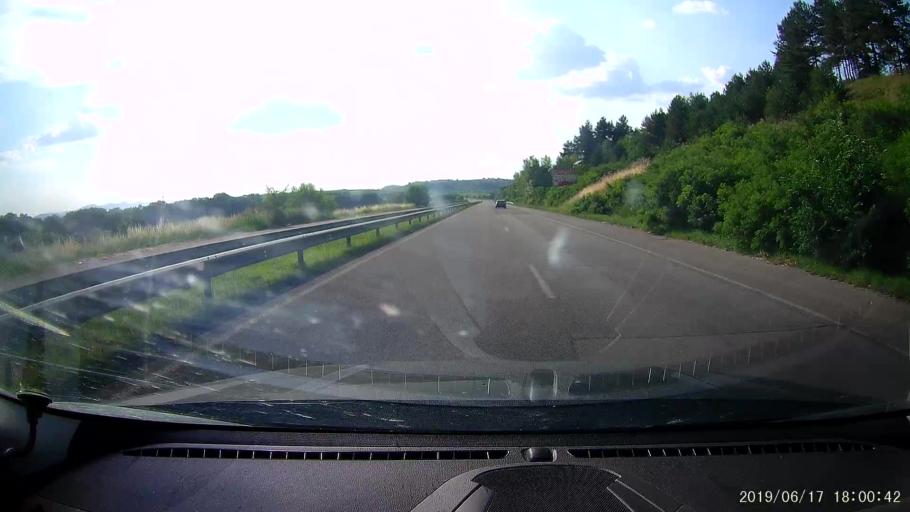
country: BG
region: Khaskovo
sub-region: Obshtina Svilengrad
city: Svilengrad
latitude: 41.7395
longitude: 26.2737
